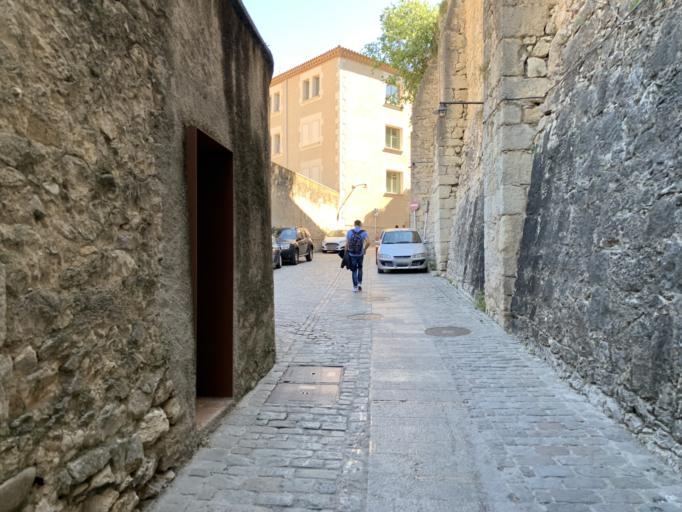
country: ES
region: Catalonia
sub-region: Provincia de Girona
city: Girona
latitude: 41.9845
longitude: 2.8274
